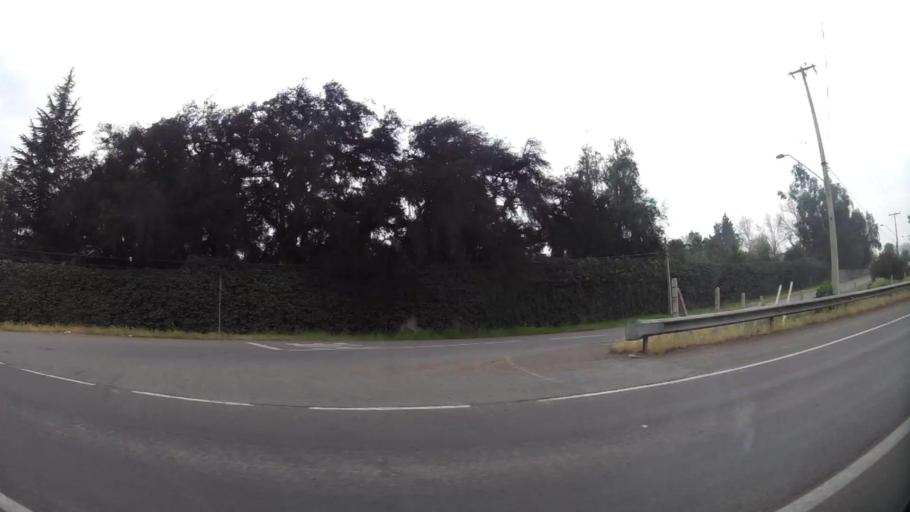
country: CL
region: Santiago Metropolitan
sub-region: Provincia de Chacabuco
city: Chicureo Abajo
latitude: -33.2426
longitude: -70.7041
